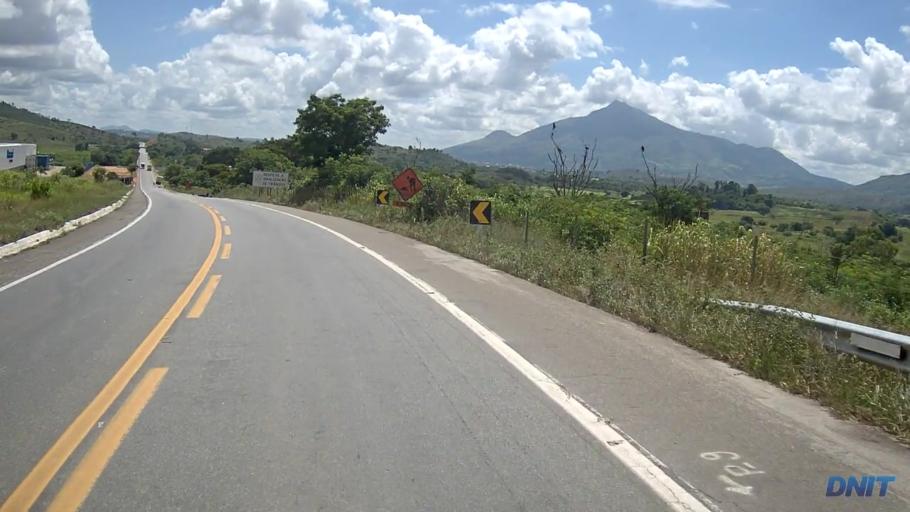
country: BR
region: Minas Gerais
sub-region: Governador Valadares
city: Governador Valadares
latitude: -18.9243
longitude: -42.0187
